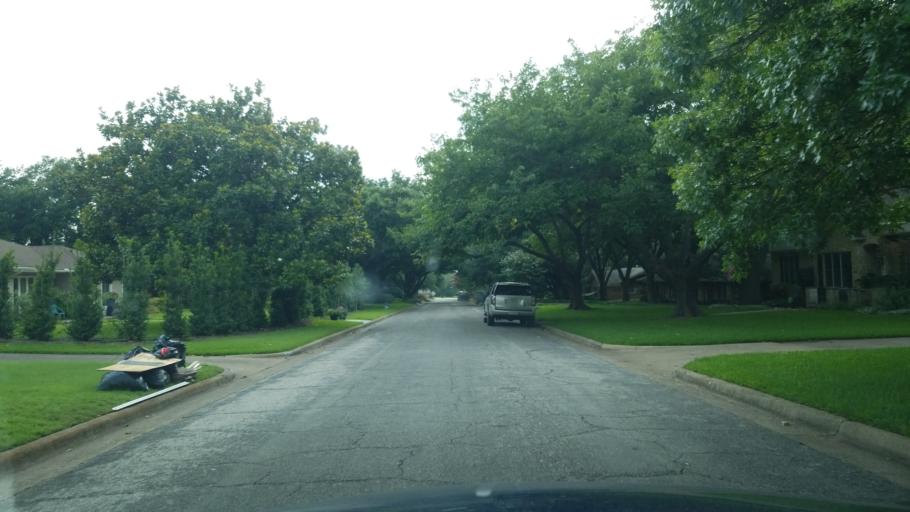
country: US
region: Texas
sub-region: Dallas County
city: Addison
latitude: 32.9110
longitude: -96.8357
